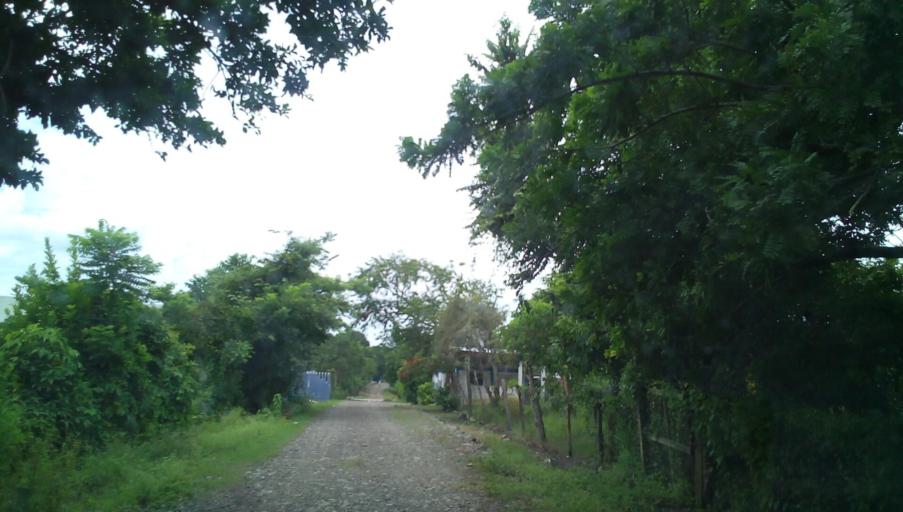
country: MX
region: Veracruz
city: Tepetzintla
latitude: 21.1285
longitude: -97.8554
